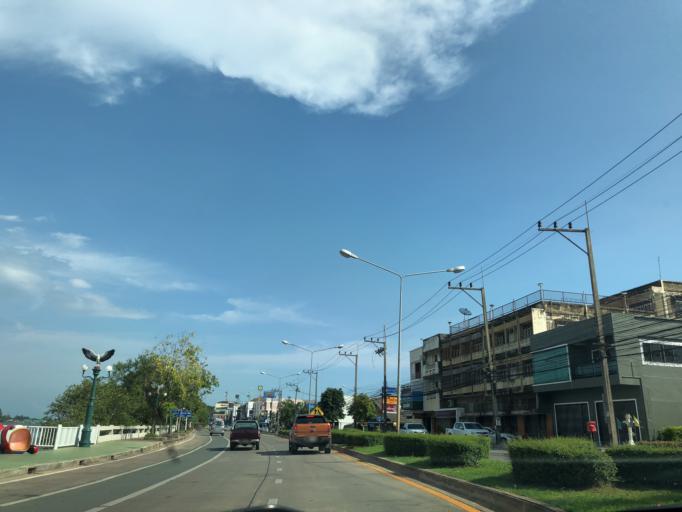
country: TH
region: Krabi
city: Krabi
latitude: 8.0691
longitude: 98.9167
